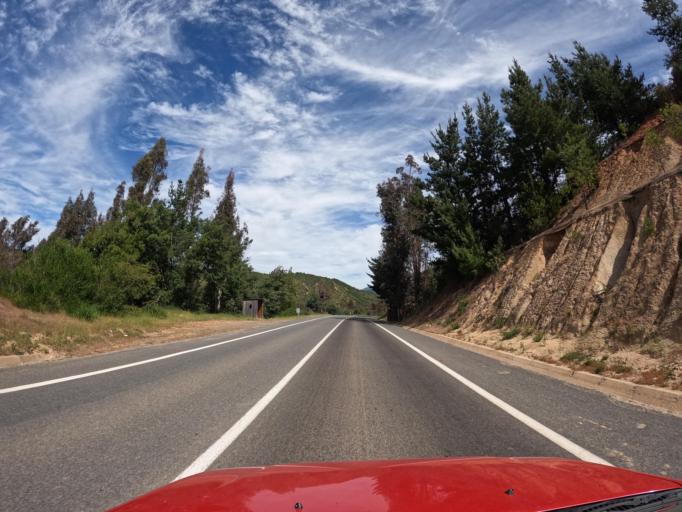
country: CL
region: Maule
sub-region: Provincia de Talca
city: Talca
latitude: -35.1521
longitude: -71.9618
